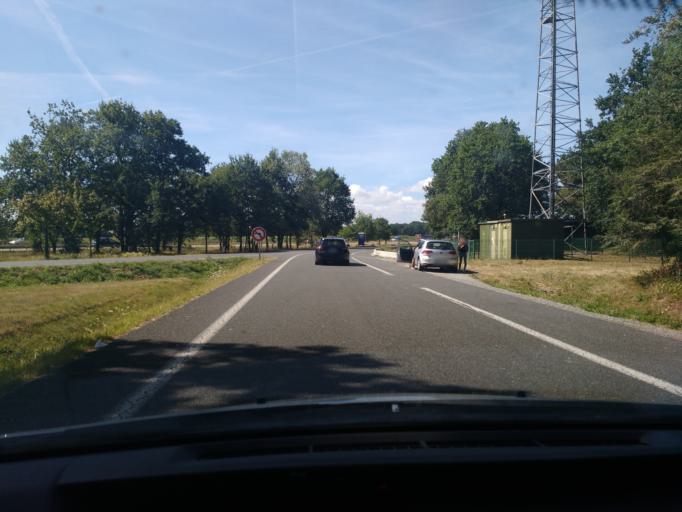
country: FR
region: Pays de la Loire
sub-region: Departement de la Loire-Atlantique
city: Saint-Mars-du-Desert
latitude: 47.3394
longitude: -1.3841
